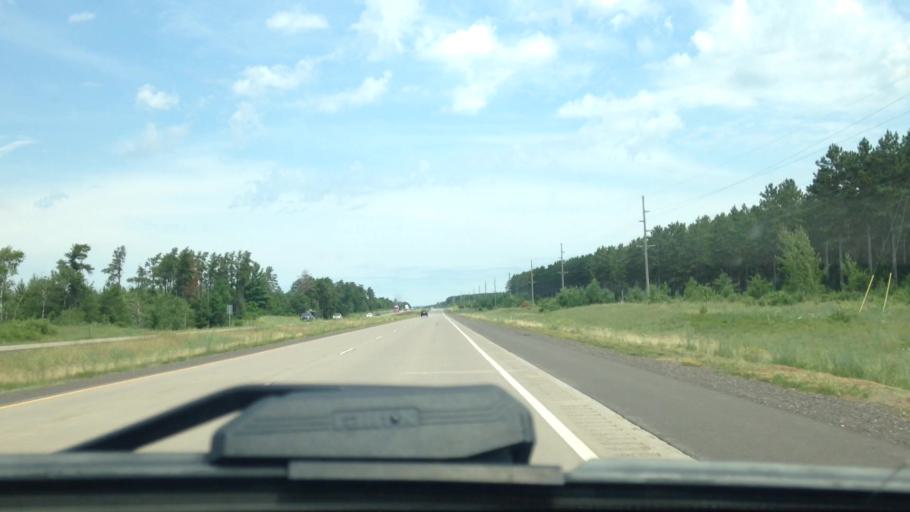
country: US
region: Wisconsin
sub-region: Douglas County
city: Lake Nebagamon
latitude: 46.2891
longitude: -91.8113
